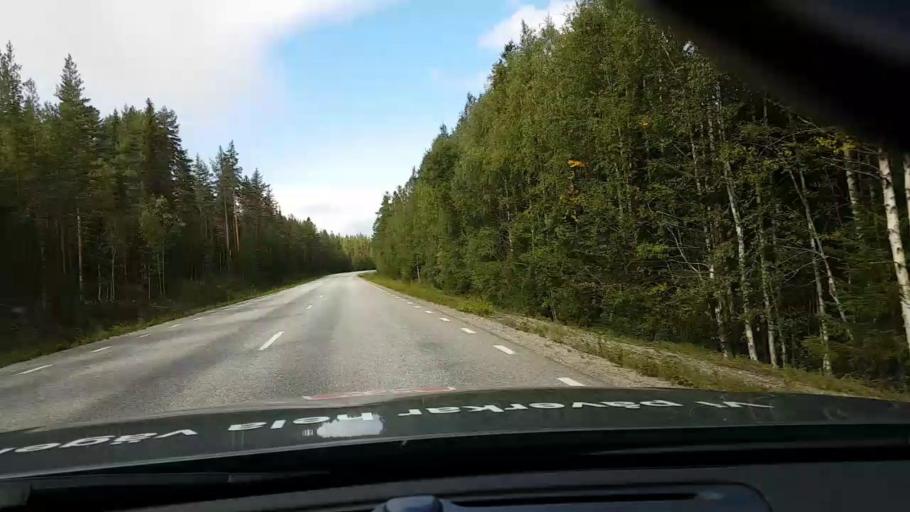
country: SE
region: Vaesternorrland
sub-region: OErnskoeldsviks Kommun
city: Bredbyn
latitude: 63.6029
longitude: 17.9052
